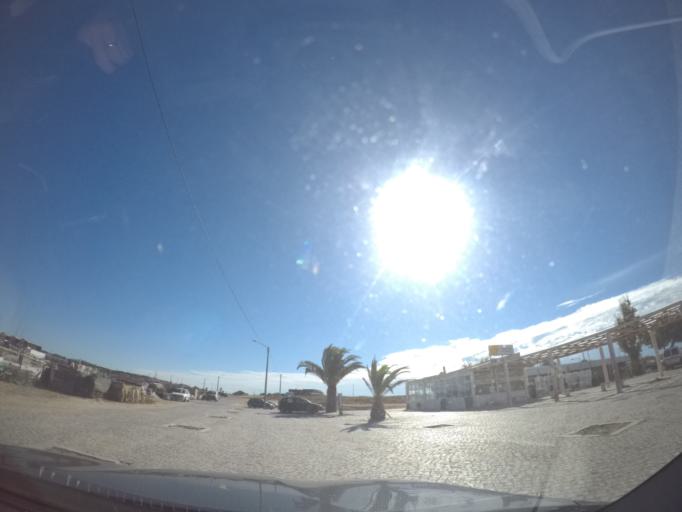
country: PT
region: Faro
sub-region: Lagos
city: Lagos
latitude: 37.1039
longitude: -8.6702
